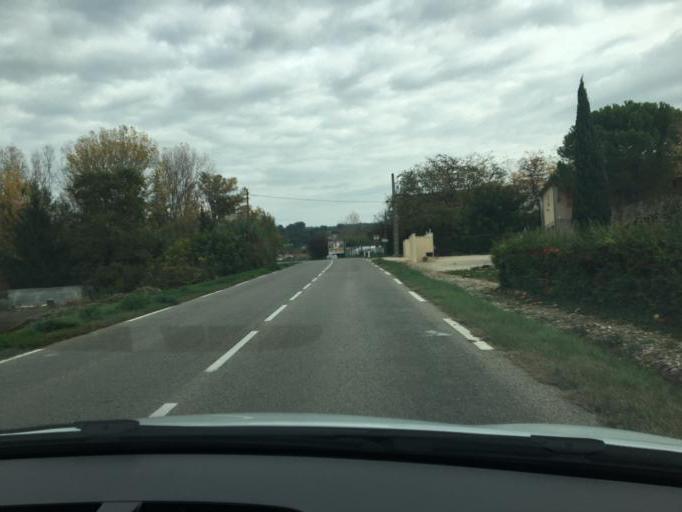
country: FR
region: Provence-Alpes-Cote d'Azur
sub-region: Departement du Vaucluse
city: Visan
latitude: 44.3077
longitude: 4.9469
